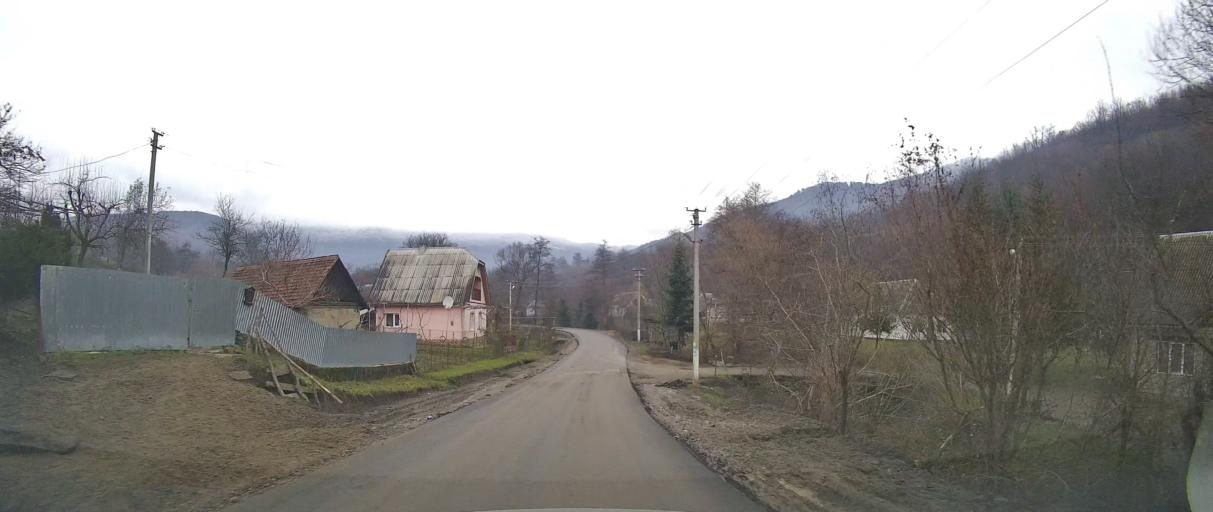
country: UA
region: Zakarpattia
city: Velykyi Bereznyi
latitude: 48.9660
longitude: 22.5512
